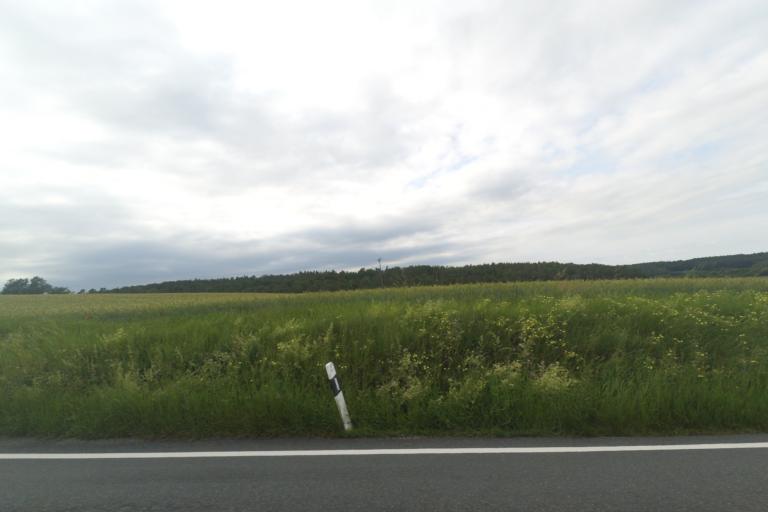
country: DE
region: Bavaria
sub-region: Upper Franconia
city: Schlusselfeld
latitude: 49.7792
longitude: 10.6517
